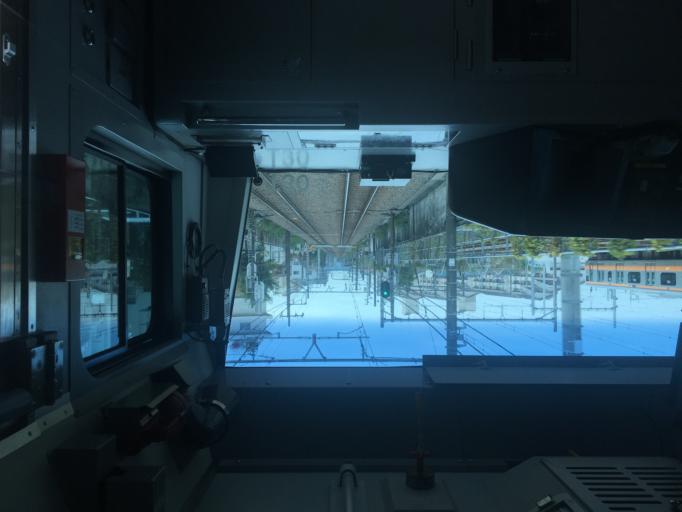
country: JP
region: Tokyo
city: Fussa
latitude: 35.7172
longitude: 139.3491
